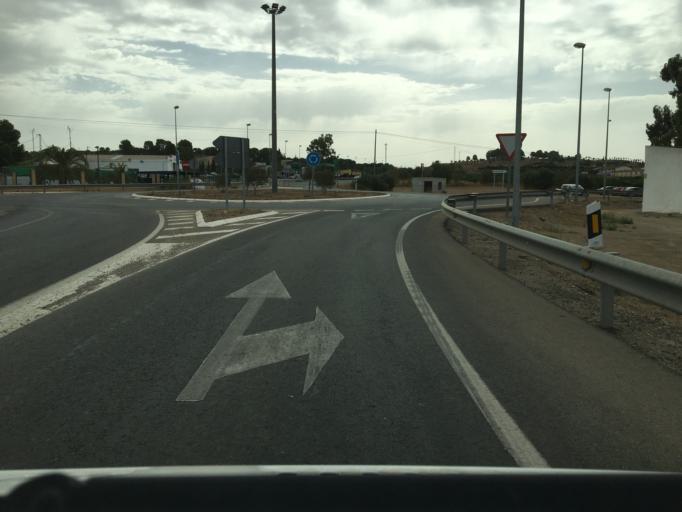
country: ES
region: Andalusia
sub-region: Provincia de Almeria
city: Huercal-Overa
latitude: 37.4170
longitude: -1.8787
